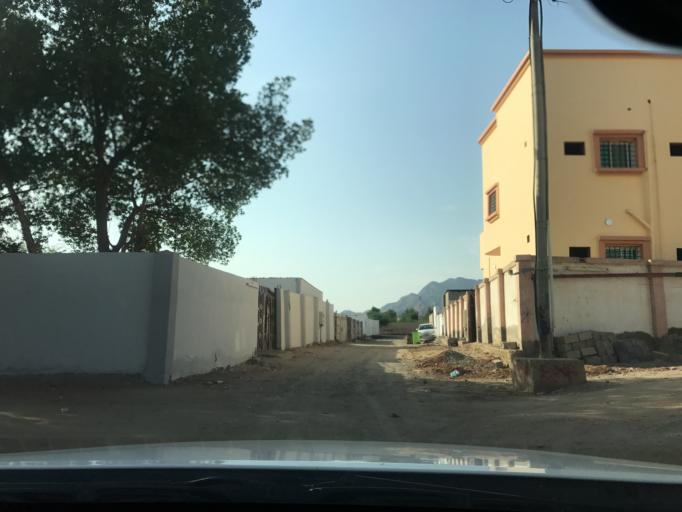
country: SA
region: Makkah
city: Al Jumum
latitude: 21.4373
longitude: 39.5198
